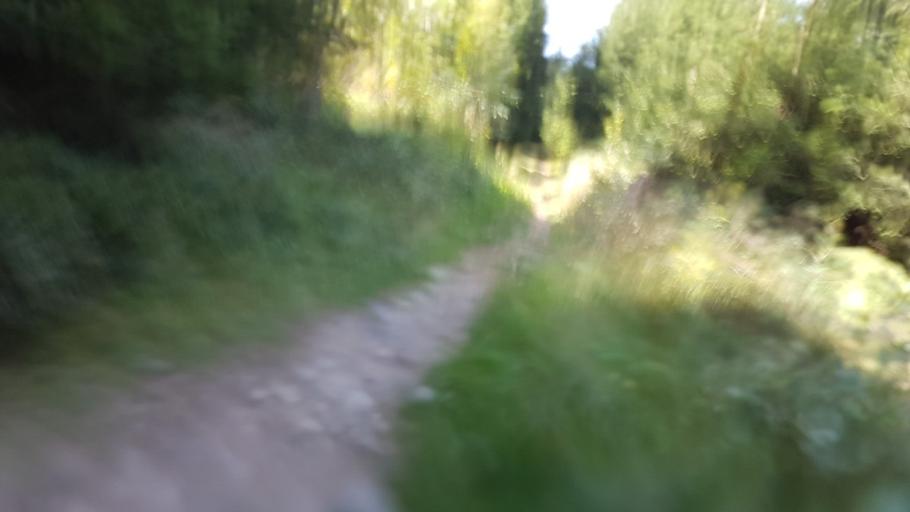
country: CH
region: Bern
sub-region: Thun District
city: Buchholterberg
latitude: 46.8254
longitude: 7.6677
